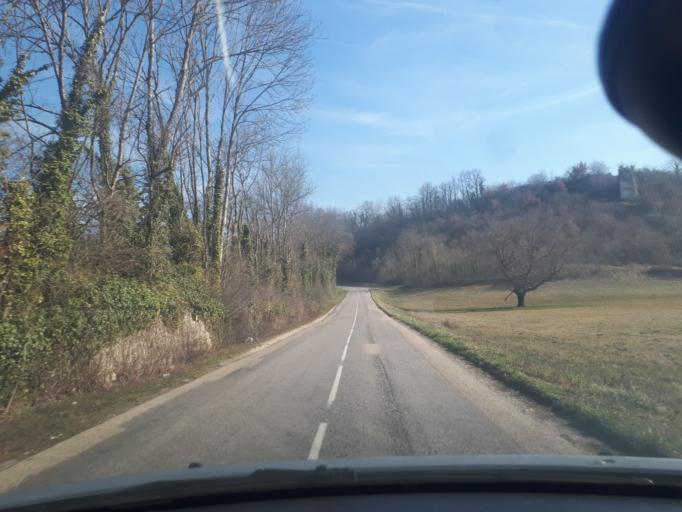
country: FR
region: Rhone-Alpes
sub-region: Departement de l'Isere
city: Sermerieu
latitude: 45.6705
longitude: 5.3927
